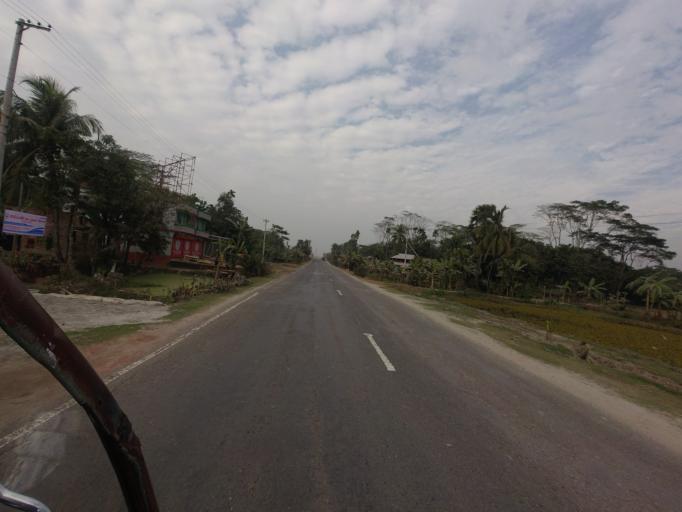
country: BD
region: Barisal
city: Nalchiti
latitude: 22.4556
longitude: 90.3407
